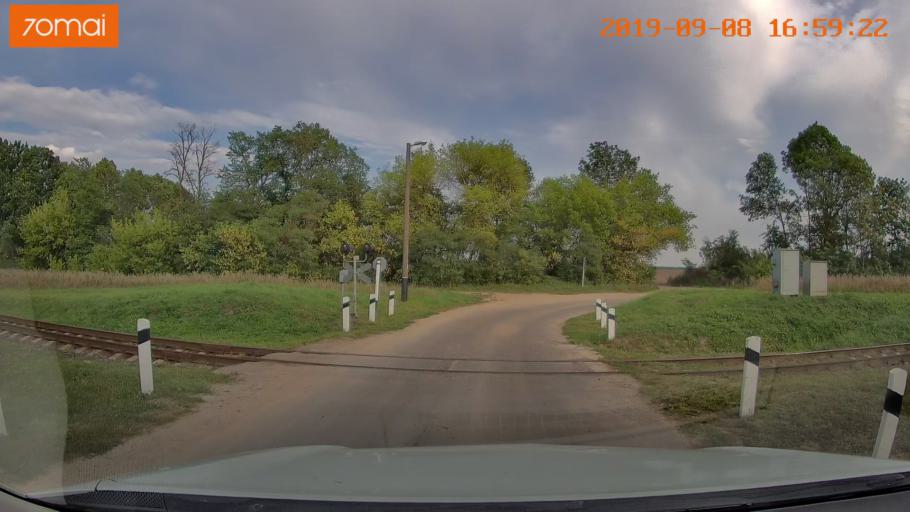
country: BY
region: Grodnenskaya
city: Hrodna
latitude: 53.7234
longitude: 23.9334
